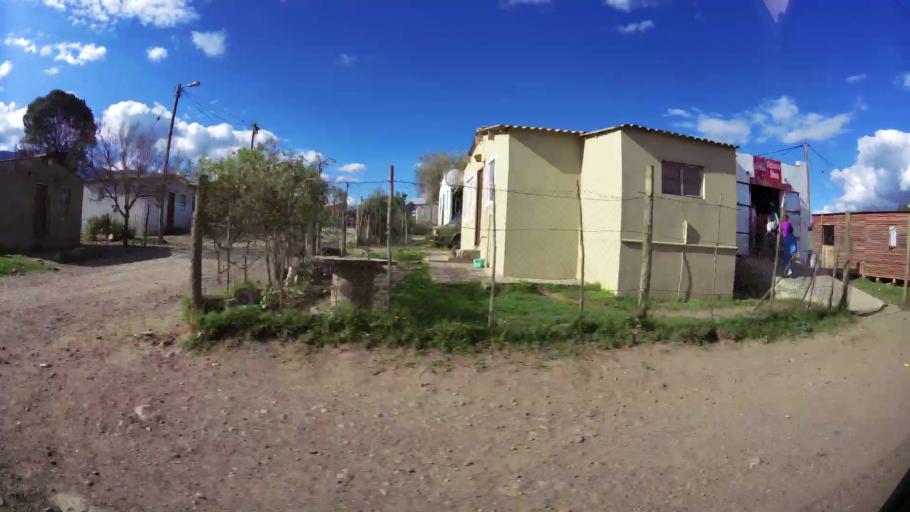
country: ZA
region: Western Cape
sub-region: Overberg District Municipality
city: Swellendam
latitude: -34.0436
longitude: 20.4450
